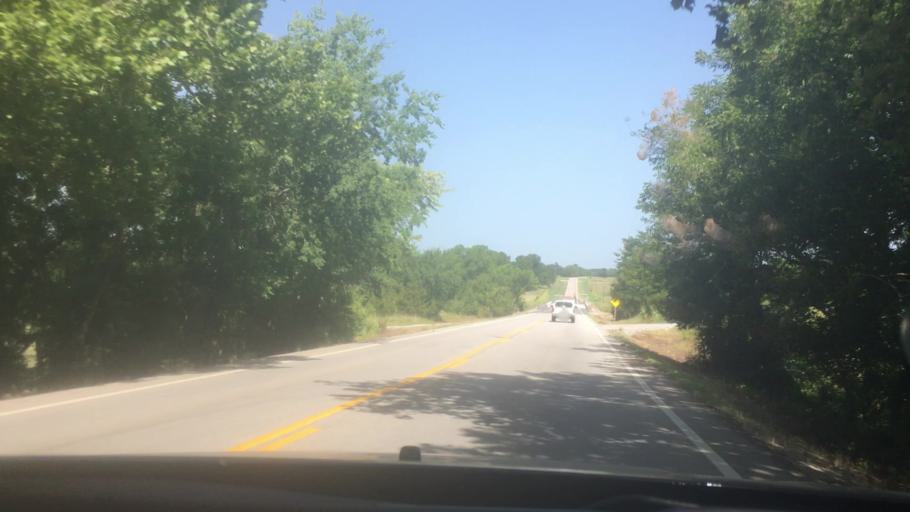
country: US
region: Oklahoma
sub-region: Bryan County
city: Durant
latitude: 34.1677
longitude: -96.4043
